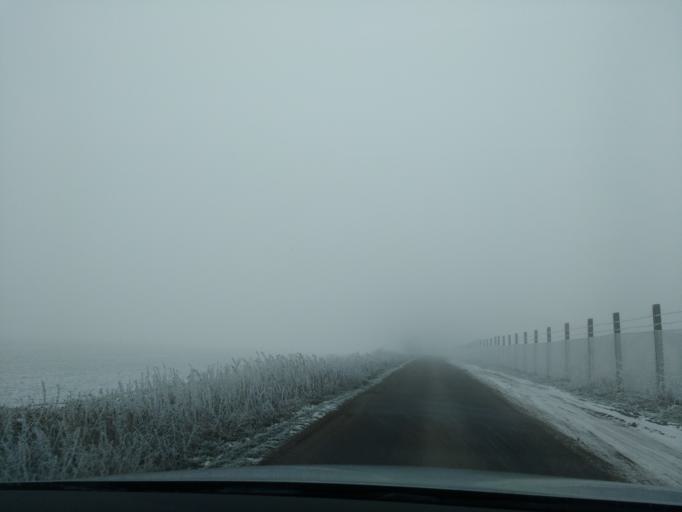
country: DE
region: Saxony-Anhalt
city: Gutenberg
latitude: 51.5676
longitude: 12.0007
